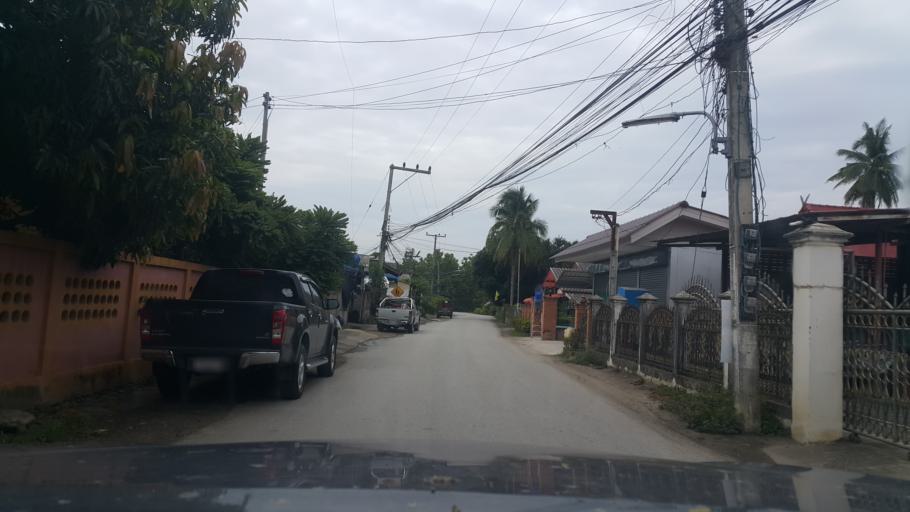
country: TH
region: Chiang Mai
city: San Pa Tong
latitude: 18.6668
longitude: 98.8345
